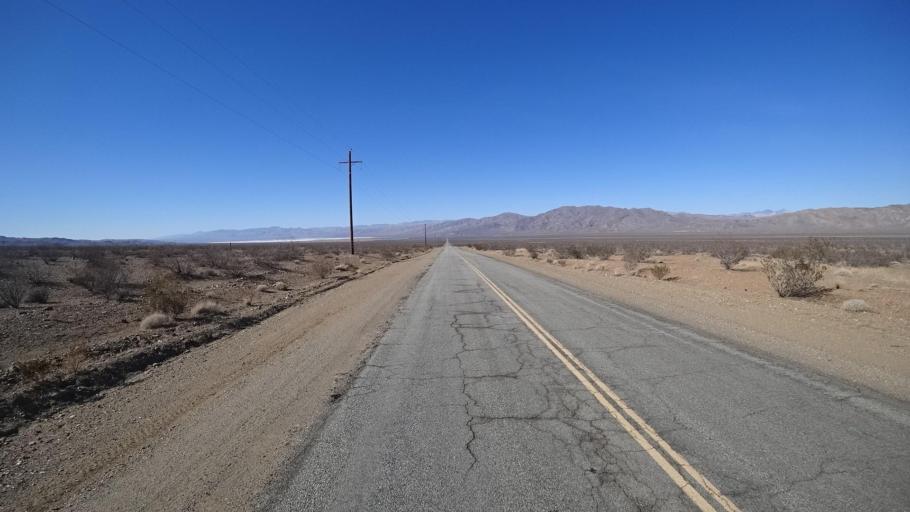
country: US
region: California
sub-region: Kern County
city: Ridgecrest
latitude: 35.3823
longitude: -117.6964
